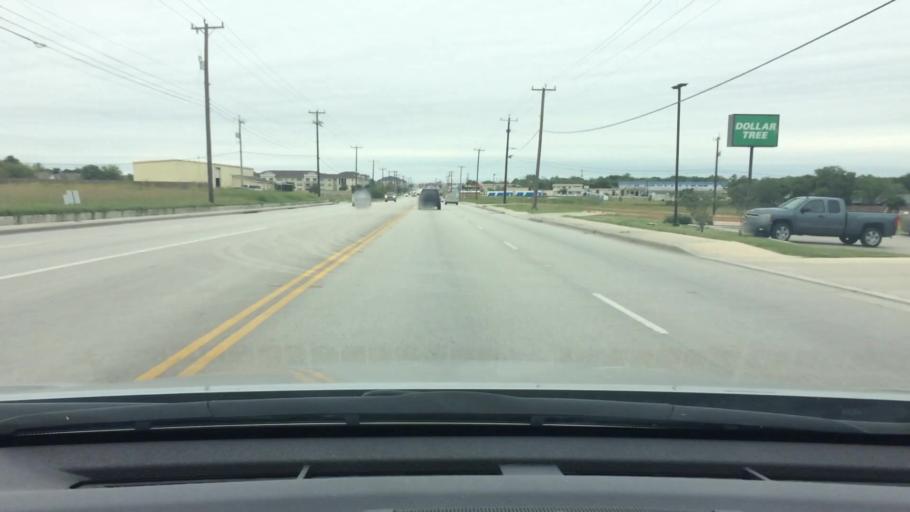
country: US
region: Texas
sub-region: Bexar County
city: Kirby
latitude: 29.4686
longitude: -98.3594
